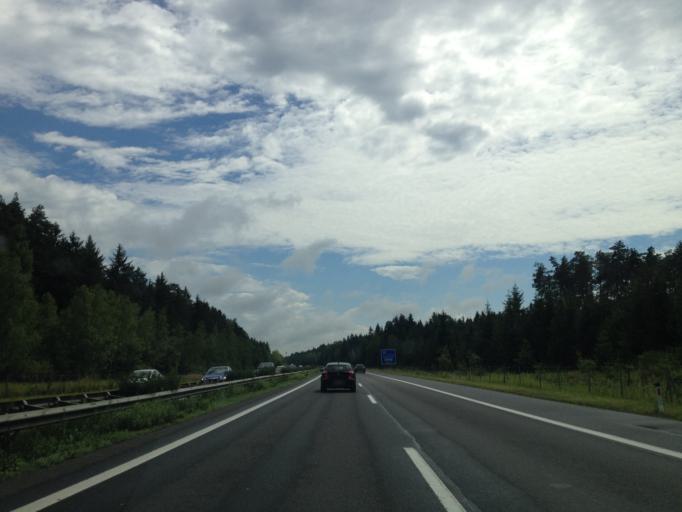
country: AT
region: Styria
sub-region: Politischer Bezirk Hartberg-Fuerstenfeld
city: Bad Waltersdorf
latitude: 47.1328
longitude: 15.9853
